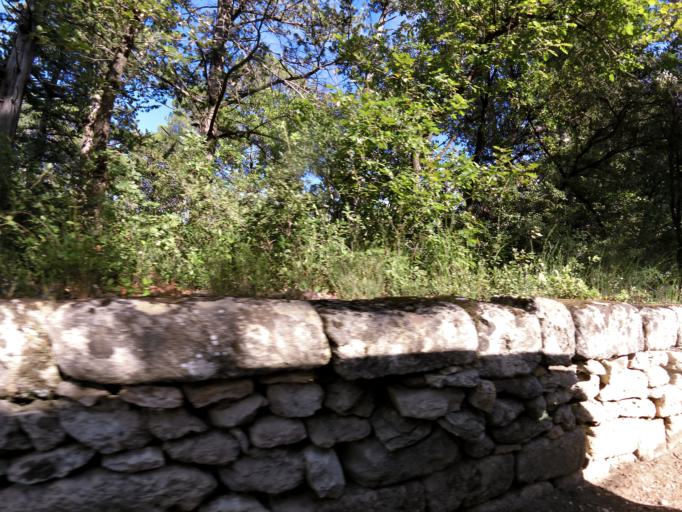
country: FR
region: Languedoc-Roussillon
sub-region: Departement du Gard
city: Villevieille
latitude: 43.8070
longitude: 4.0910
